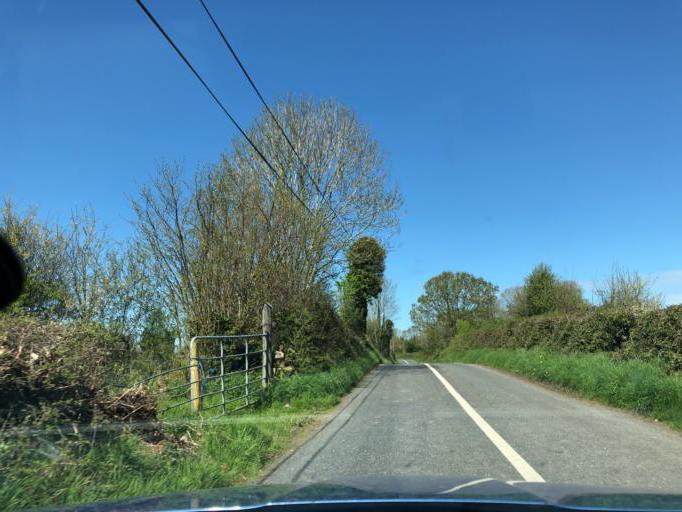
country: IE
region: Connaught
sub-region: County Galway
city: Loughrea
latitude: 53.1620
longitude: -8.4003
